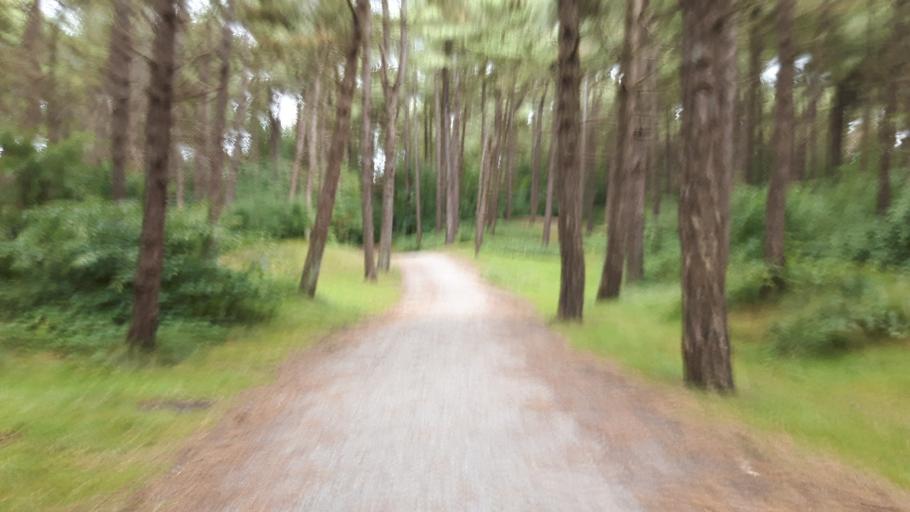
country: NL
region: Friesland
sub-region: Gemeente Ameland
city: Hollum
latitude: 53.4474
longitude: 5.6250
